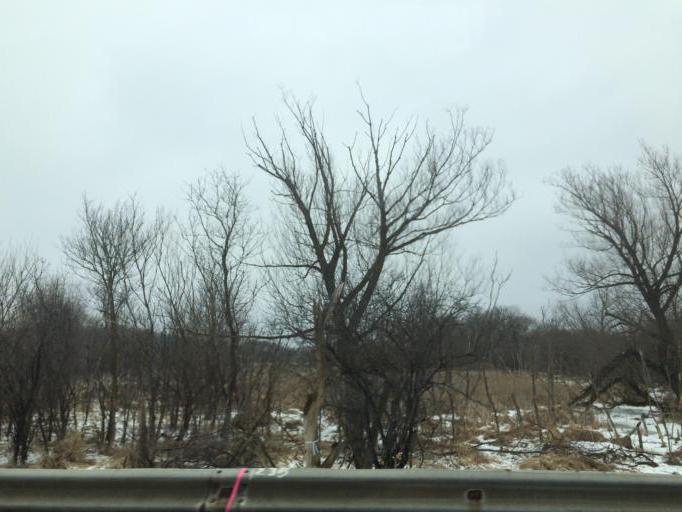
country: US
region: Illinois
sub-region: McHenry County
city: Huntley
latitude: 42.2300
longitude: -88.4225
